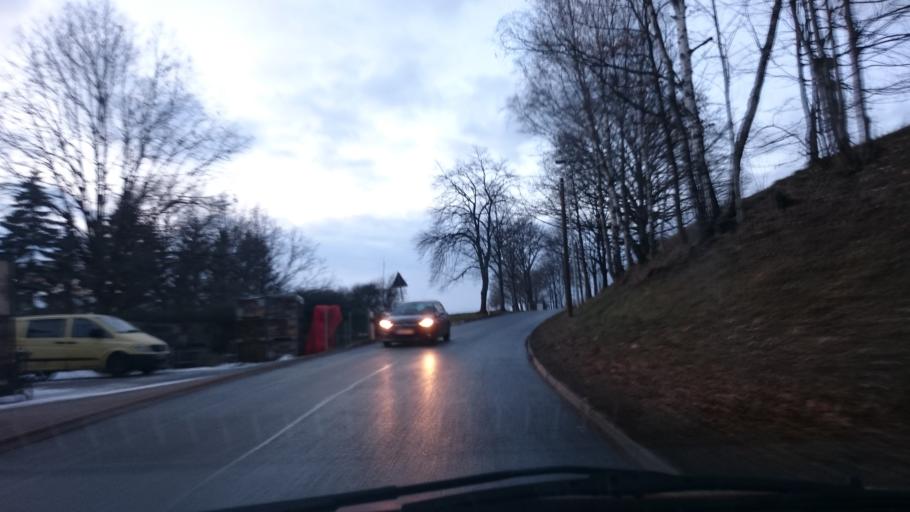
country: DE
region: Saxony
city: Wilkau-Hasslau
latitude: 50.7061
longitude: 12.5128
